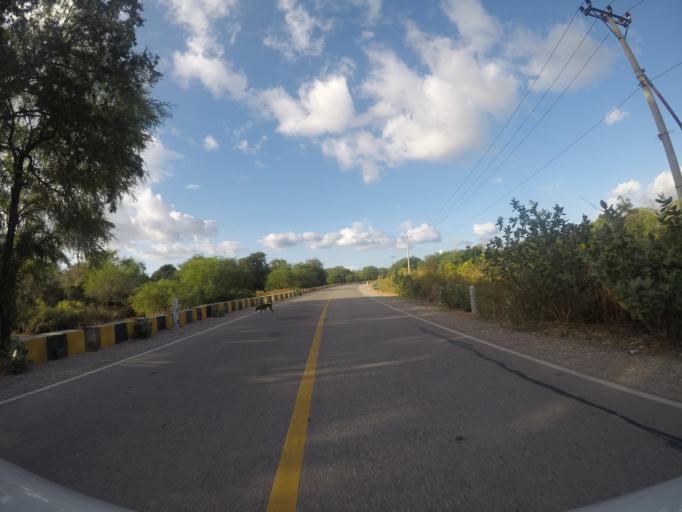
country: TL
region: Lautem
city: Lospalos
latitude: -8.3696
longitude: 126.8951
